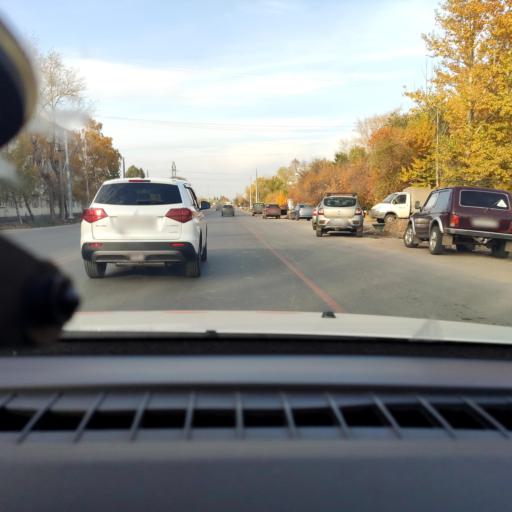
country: RU
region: Samara
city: Samara
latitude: 53.1229
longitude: 50.0883
